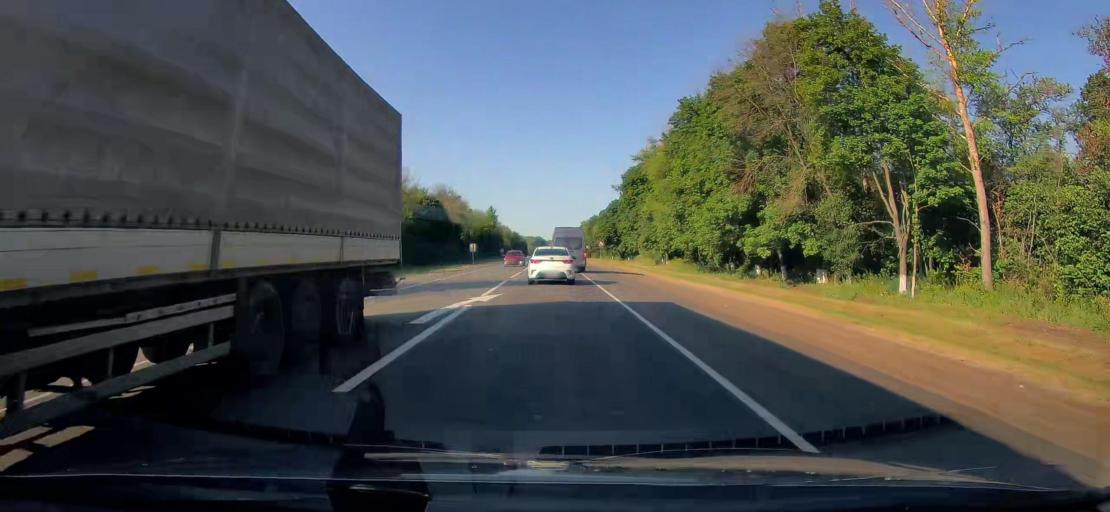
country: RU
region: Orjol
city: Mtsensk
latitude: 53.2043
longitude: 36.4448
